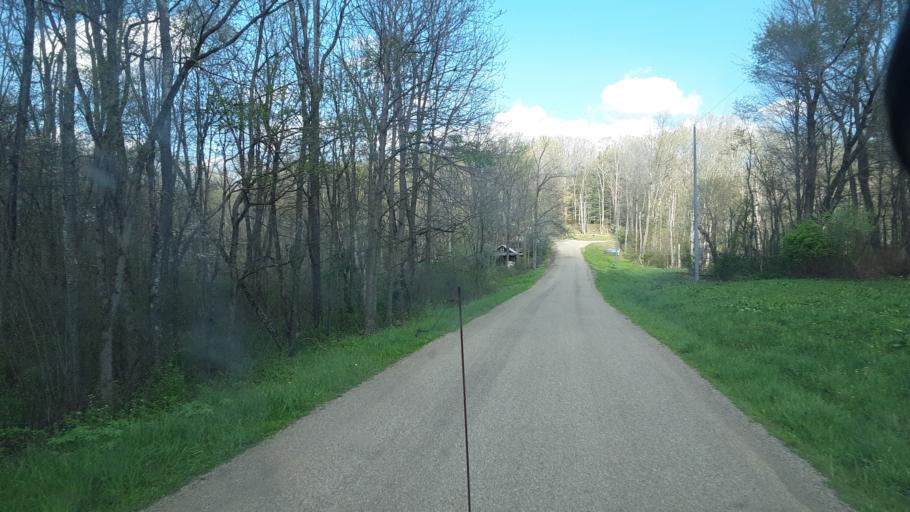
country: US
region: Ohio
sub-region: Ashland County
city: Loudonville
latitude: 40.5730
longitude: -82.3396
